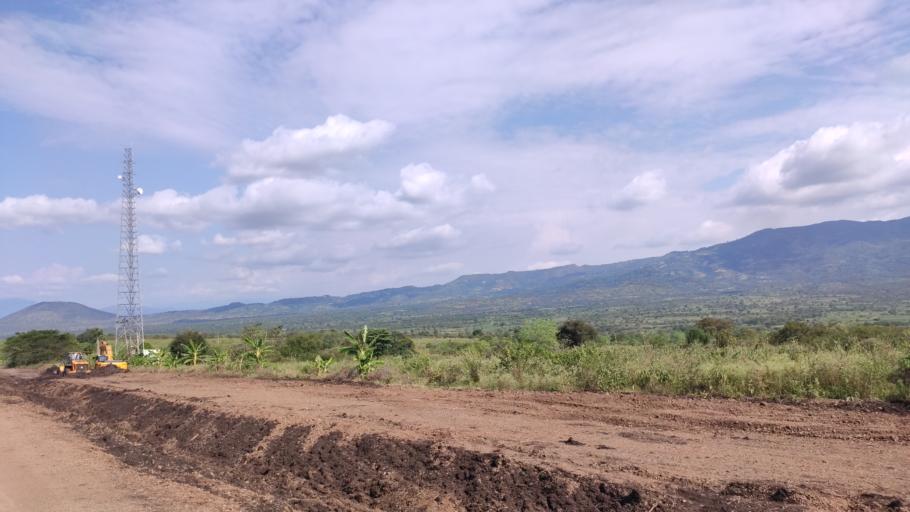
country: ET
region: Southern Nations, Nationalities, and People's Region
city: Felege Neway
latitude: 6.3966
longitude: 37.1093
